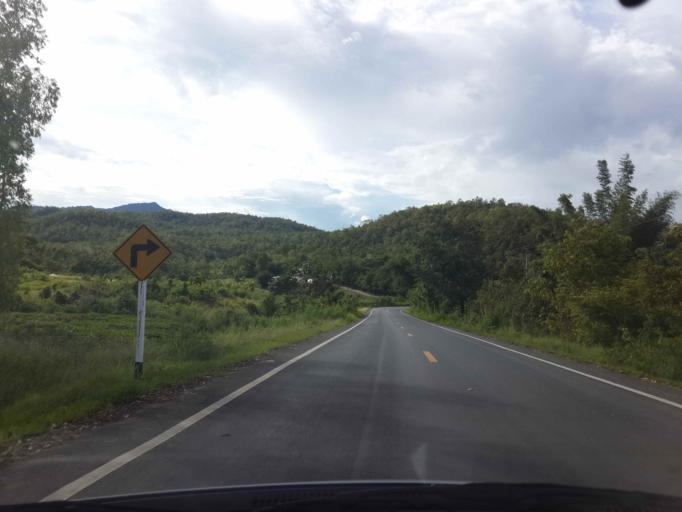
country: TH
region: Kanchanaburi
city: Dan Makham Tia
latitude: 13.8222
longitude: 99.1686
